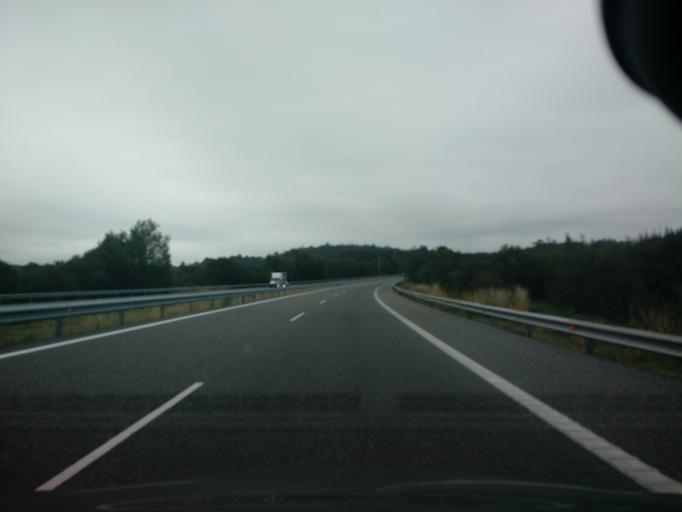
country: ES
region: Galicia
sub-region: Provincia da Coruna
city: Santiago de Compostela
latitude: 42.9155
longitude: -8.4773
